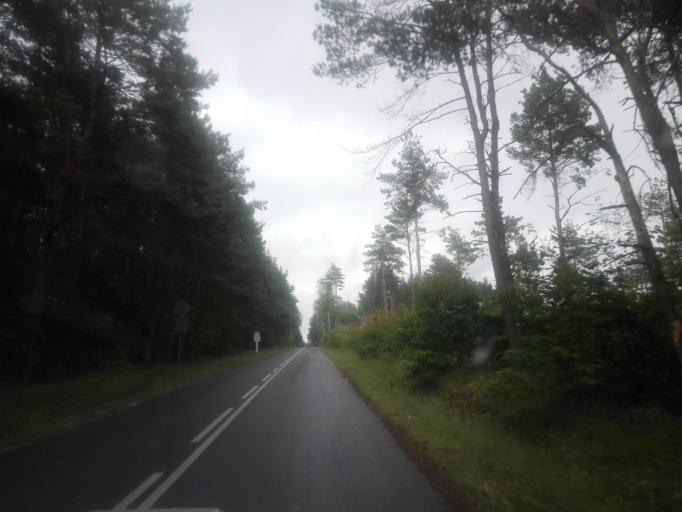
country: PL
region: Silesian Voivodeship
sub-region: Powiat myszkowski
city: Choron
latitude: 50.7078
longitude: 19.3396
